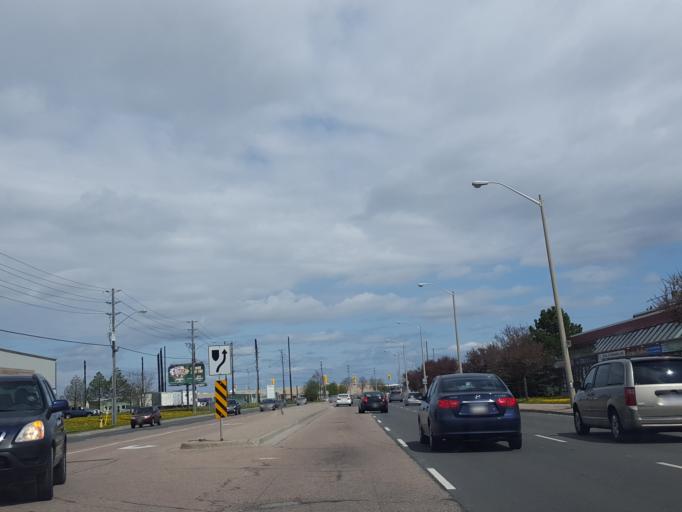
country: CA
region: Ontario
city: Markham
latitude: 43.8285
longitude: -79.2497
